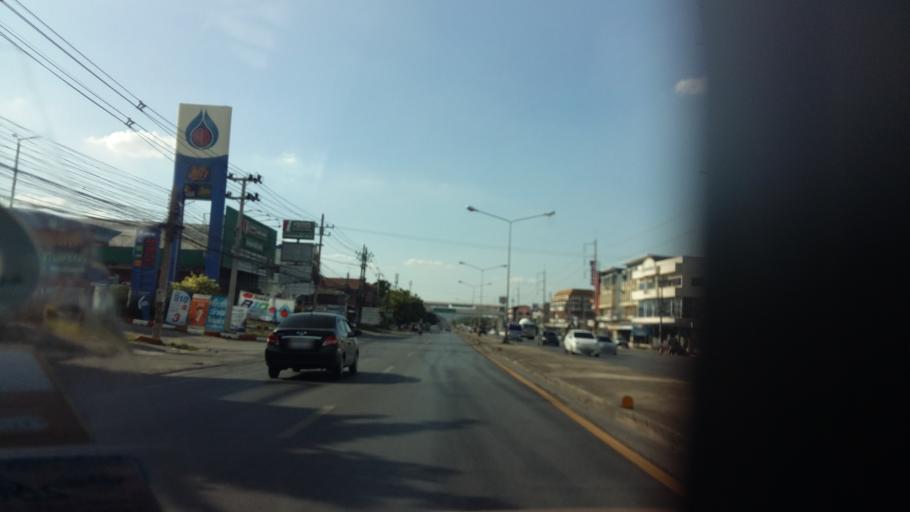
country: TH
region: Lop Buri
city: Lop Buri
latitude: 14.8249
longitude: 100.6474
